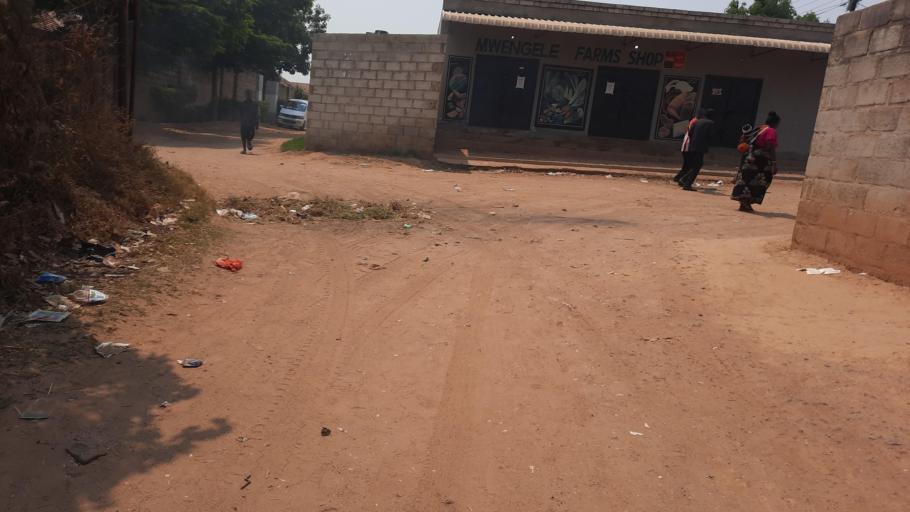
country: ZM
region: Lusaka
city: Lusaka
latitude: -15.4065
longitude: 28.3806
